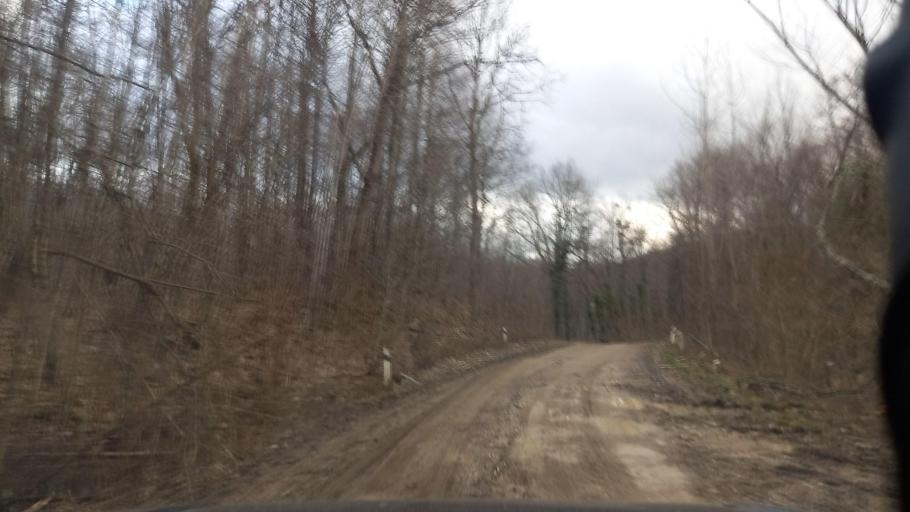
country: RU
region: Krasnodarskiy
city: Dzhubga
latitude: 44.4864
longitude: 38.7825
